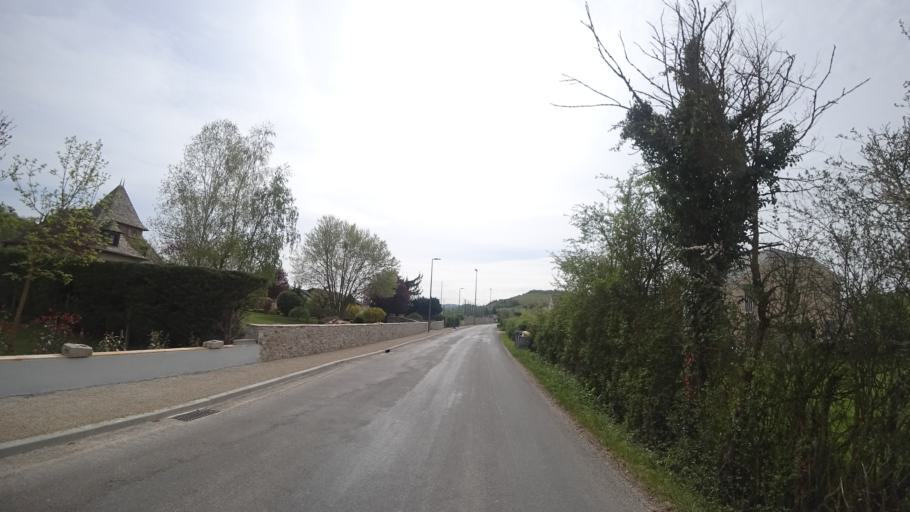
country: FR
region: Midi-Pyrenees
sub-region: Departement de l'Aveyron
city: Sebazac-Concoures
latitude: 44.3781
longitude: 2.6048
